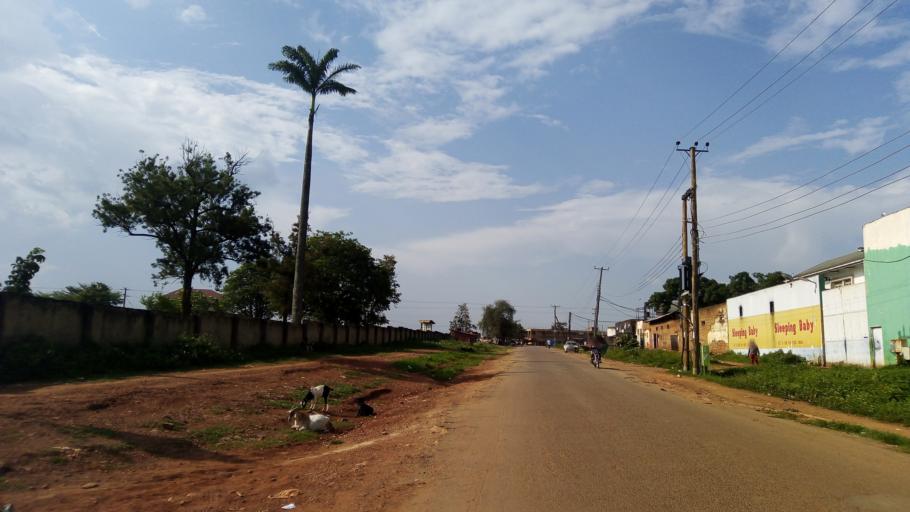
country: UG
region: Eastern Region
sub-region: Mbale District
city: Mbale
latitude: 1.0779
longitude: 34.1607
